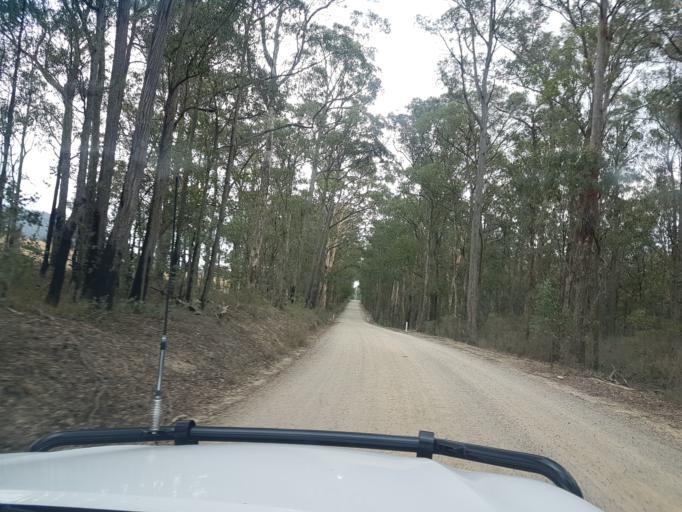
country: AU
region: Victoria
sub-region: East Gippsland
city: Bairnsdale
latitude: -37.6881
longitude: 147.5615
